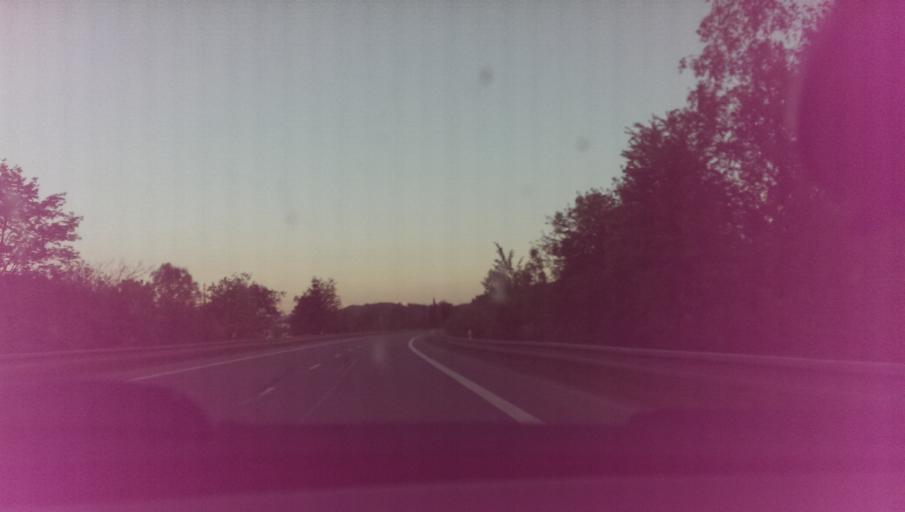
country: CZ
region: Zlin
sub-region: Okres Vsetin
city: Vsetin
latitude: 49.3532
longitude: 17.9693
